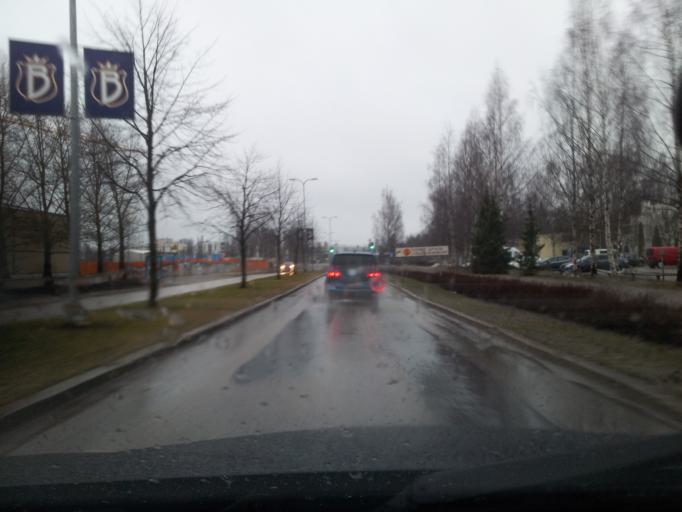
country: FI
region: Uusimaa
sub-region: Helsinki
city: Koukkuniemi
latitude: 60.1759
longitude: 24.7787
